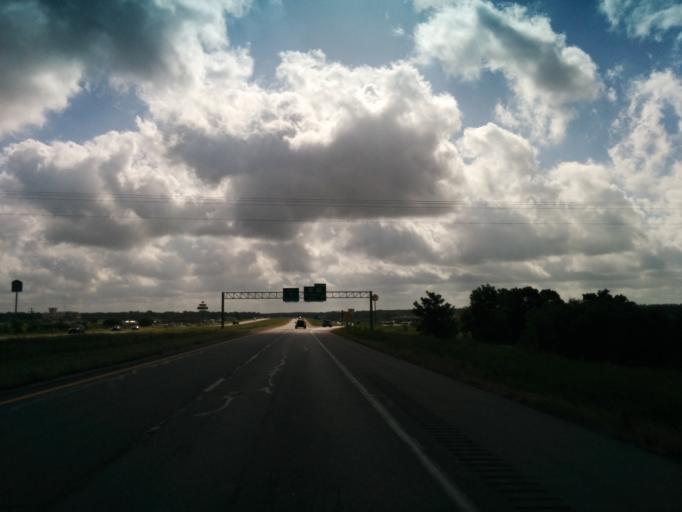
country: US
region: Texas
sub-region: Caldwell County
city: Luling
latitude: 29.6512
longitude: -97.5994
